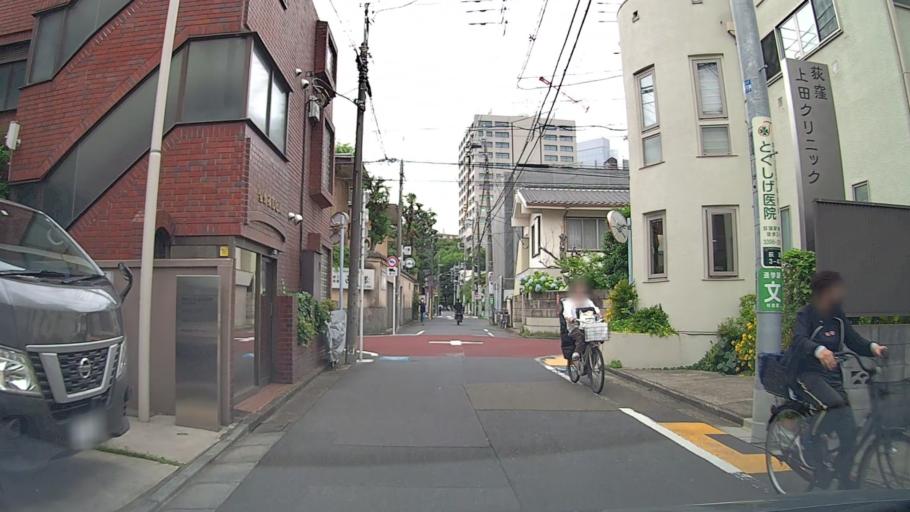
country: JP
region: Tokyo
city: Musashino
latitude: 35.7029
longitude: 139.6261
